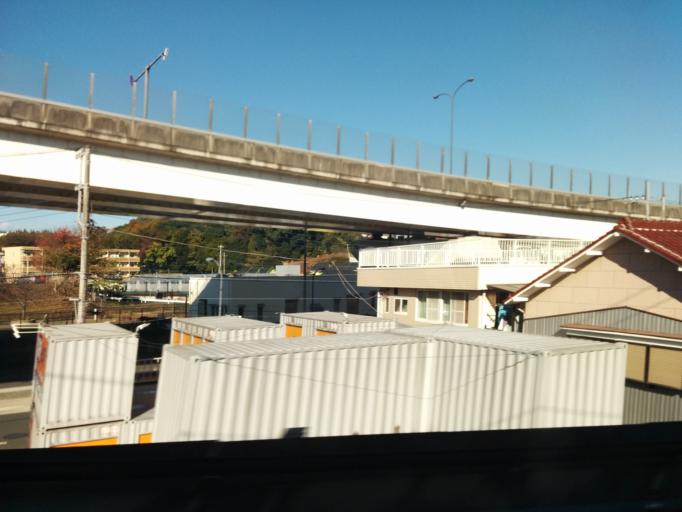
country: JP
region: Kanagawa
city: Yokohama
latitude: 35.4923
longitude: 139.5994
